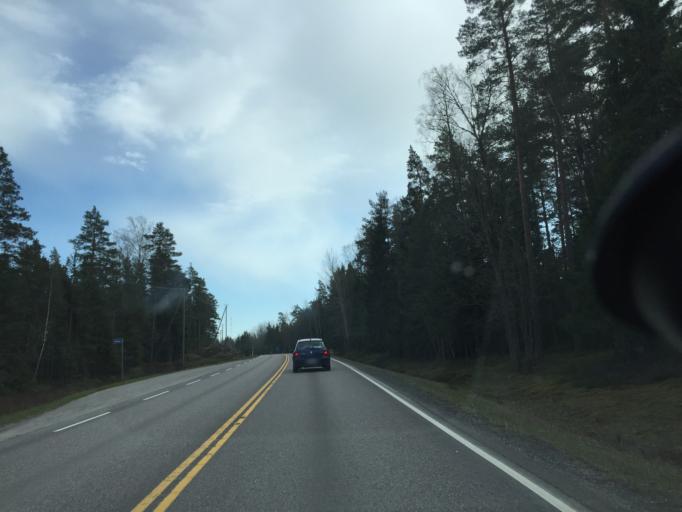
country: FI
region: Uusimaa
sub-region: Raaseporin
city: Ekenaes
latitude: 60.0288
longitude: 23.3693
